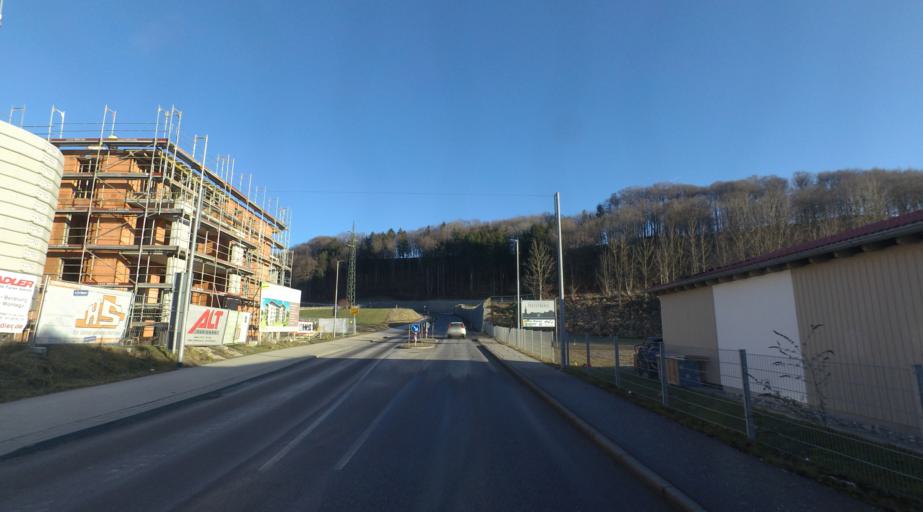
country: DE
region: Bavaria
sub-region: Upper Bavaria
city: Trostberg an der Alz
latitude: 48.0243
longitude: 12.5636
